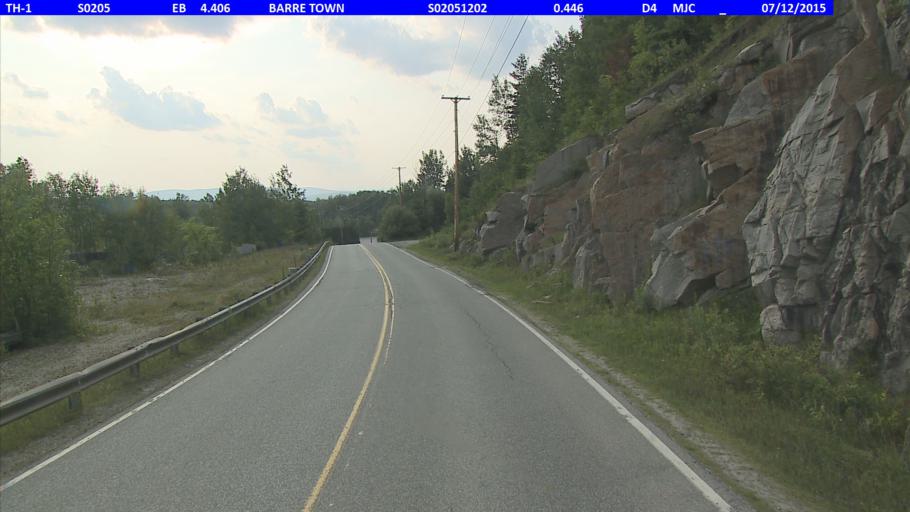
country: US
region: Vermont
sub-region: Washington County
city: South Barre
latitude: 44.1450
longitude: -72.4785
